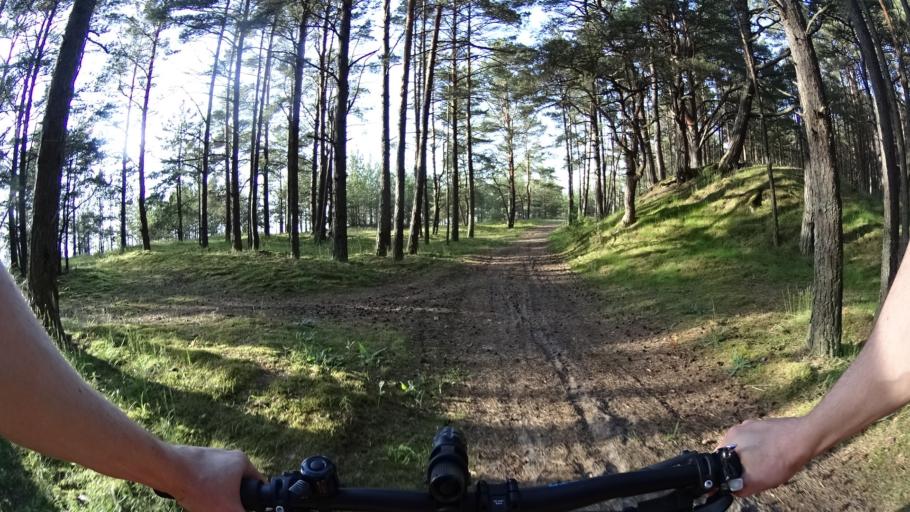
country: LV
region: Riga
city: Jaunciems
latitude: 57.0893
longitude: 24.1324
